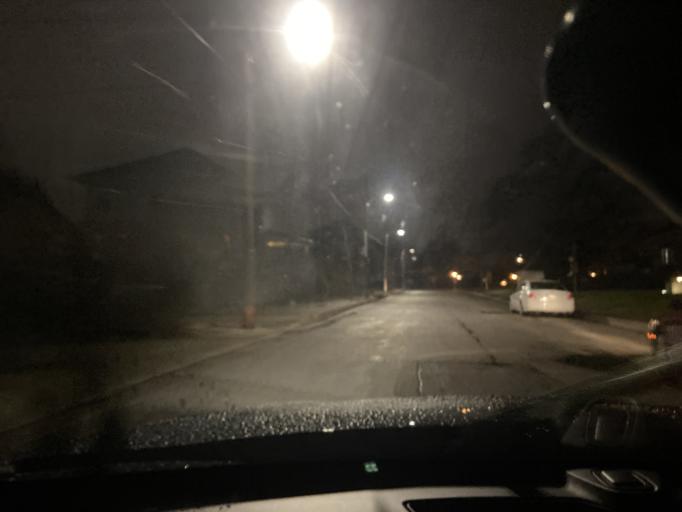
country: US
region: Maryland
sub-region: Baltimore County
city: Lochearn
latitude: 39.3330
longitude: -76.6787
